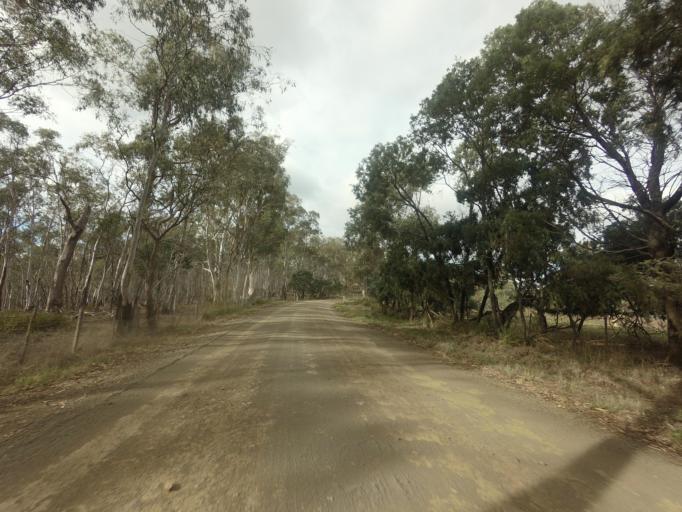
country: AU
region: Tasmania
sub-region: Brighton
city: Bridgewater
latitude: -42.4594
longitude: 147.2598
